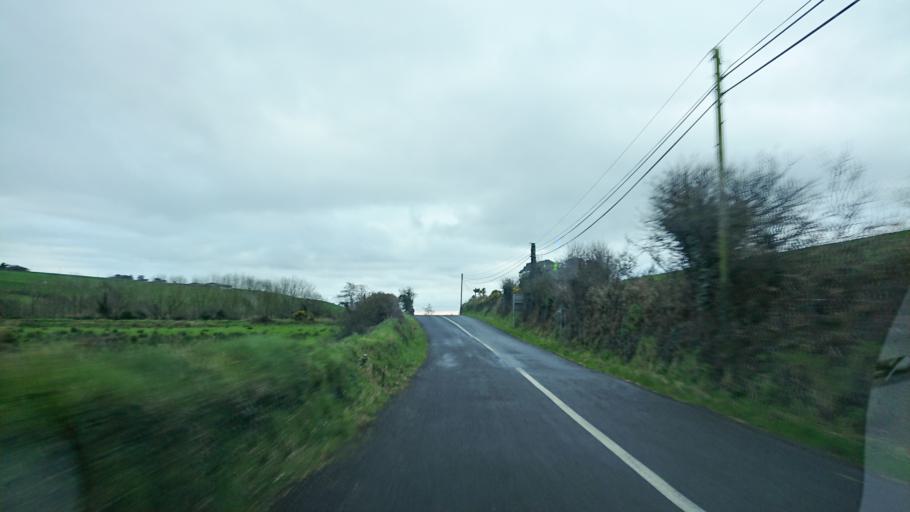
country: IE
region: Munster
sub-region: Waterford
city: Portlaw
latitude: 52.1526
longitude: -7.3810
